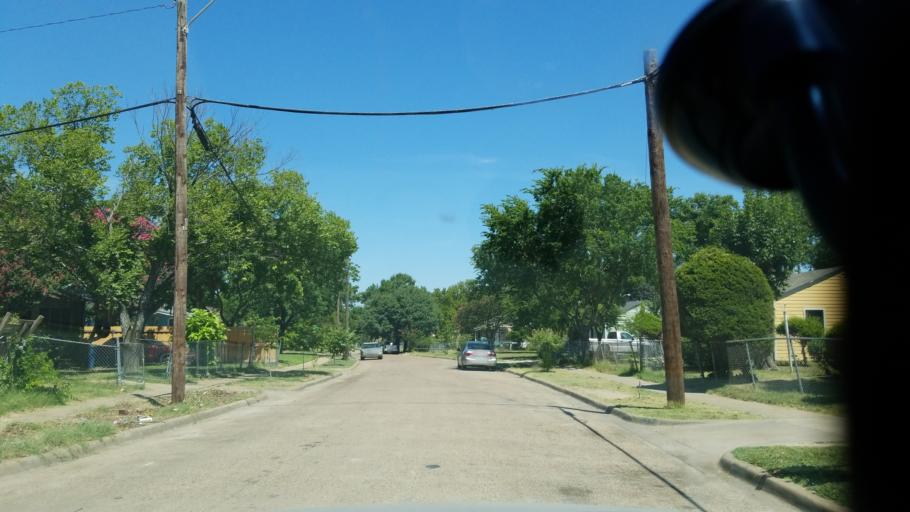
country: US
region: Texas
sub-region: Dallas County
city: Cockrell Hill
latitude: 32.7113
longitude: -96.8252
